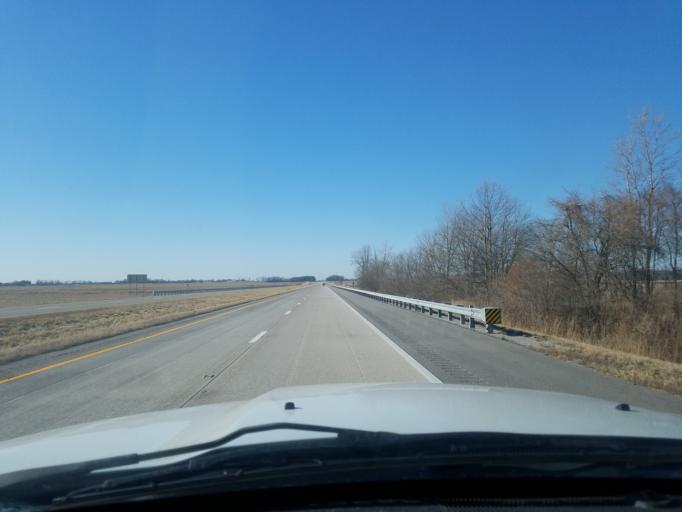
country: US
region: Kentucky
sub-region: Henderson County
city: Henderson
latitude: 37.7993
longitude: -87.5106
